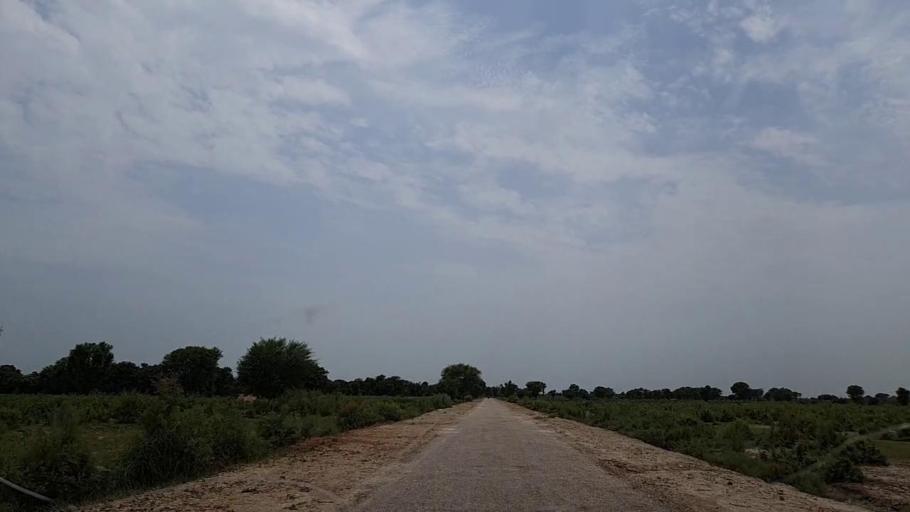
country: PK
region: Sindh
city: Tharu Shah
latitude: 26.9156
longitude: 68.0962
